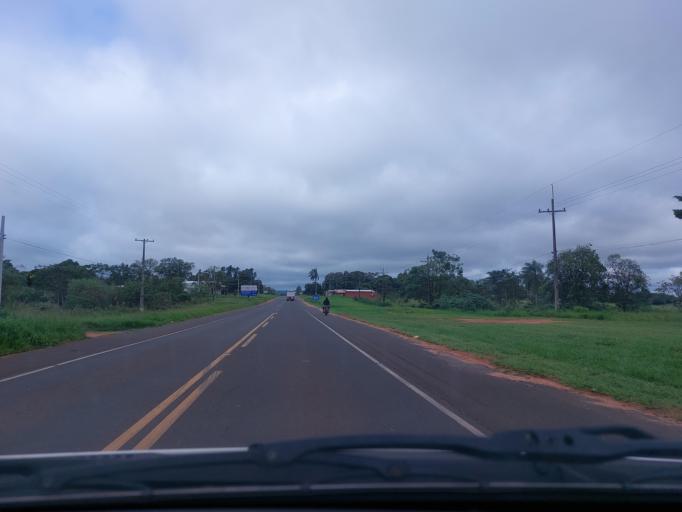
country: PY
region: San Pedro
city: Guayaybi
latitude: -24.6134
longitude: -56.3816
